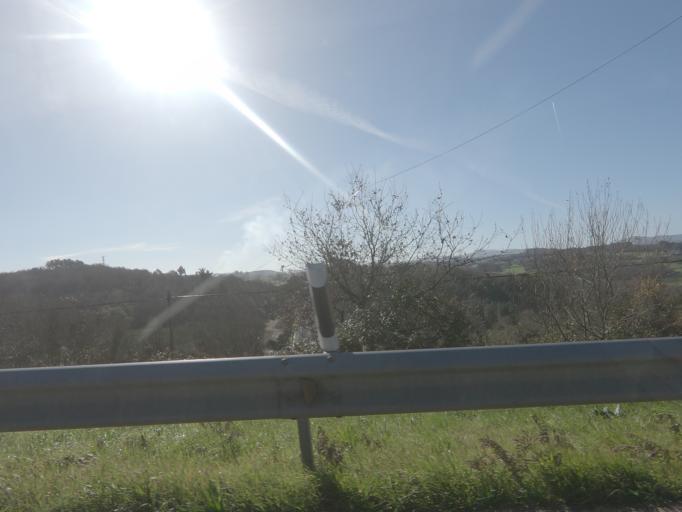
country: ES
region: Galicia
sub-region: Provincia de Pontevedra
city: Lalin
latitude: 42.6818
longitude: -8.1744
